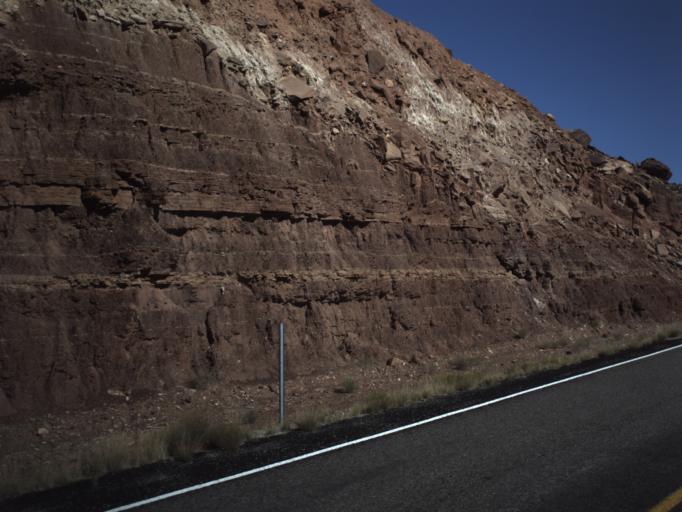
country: US
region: Utah
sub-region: San Juan County
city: Blanding
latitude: 37.8828
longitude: -110.4177
